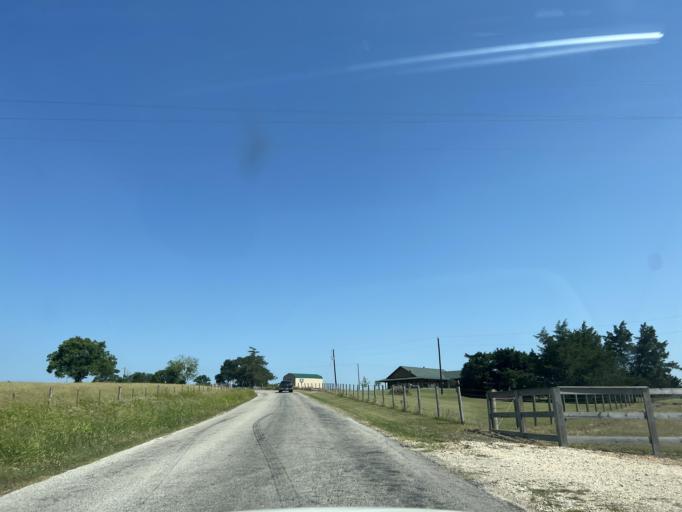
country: US
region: Texas
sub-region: Washington County
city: Brenham
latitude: 30.1643
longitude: -96.3283
